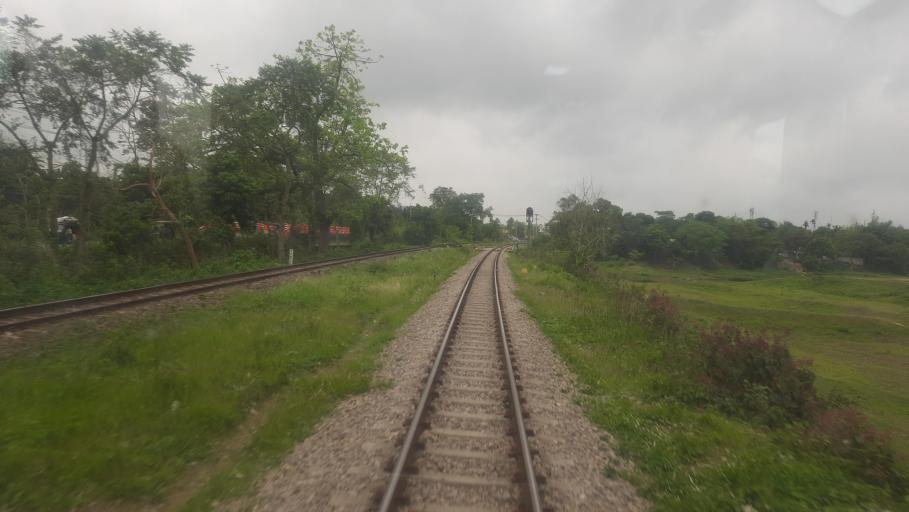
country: BD
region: Dhaka
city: Narsingdi
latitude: 23.9382
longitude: 90.7777
